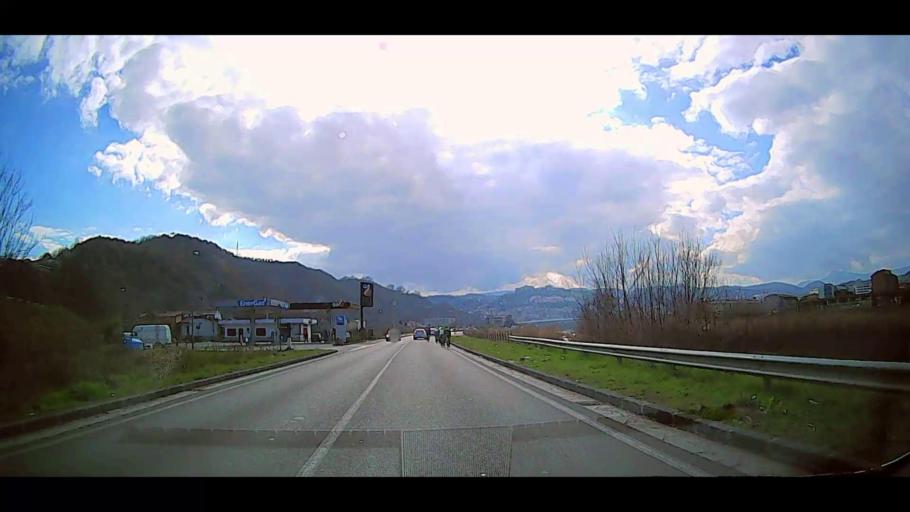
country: IT
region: Calabria
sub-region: Provincia di Cosenza
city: Cosenza
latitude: 39.3047
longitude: 16.2630
